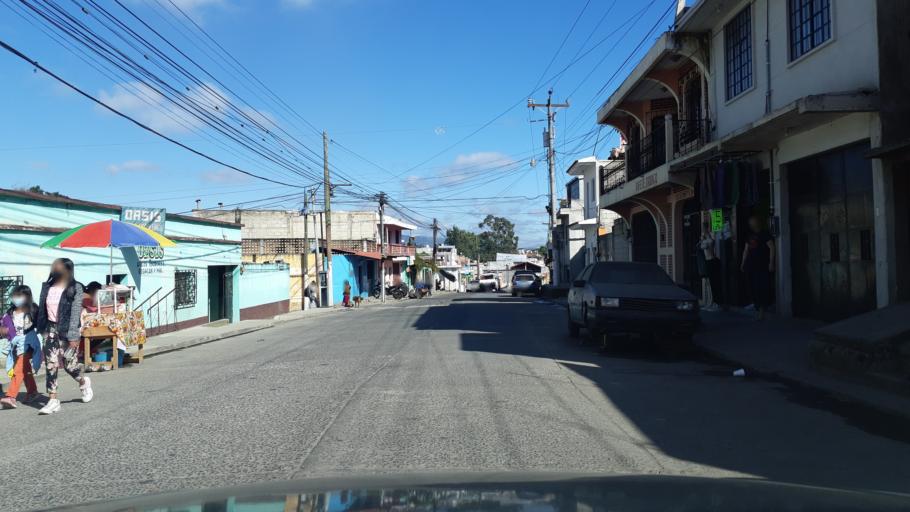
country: GT
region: Chimaltenango
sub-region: Municipio de Chimaltenango
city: Chimaltenango
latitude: 14.6564
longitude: -90.8219
